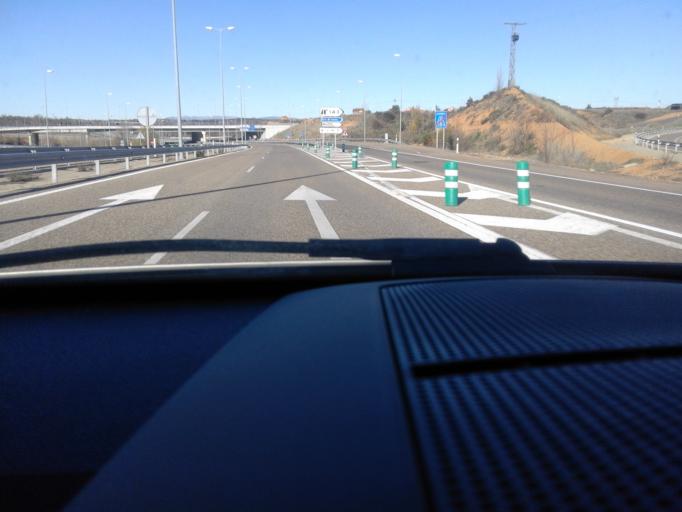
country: ES
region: Castille and Leon
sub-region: Provincia de Leon
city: Valverde de la Virgen
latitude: 42.5658
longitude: -5.6499
